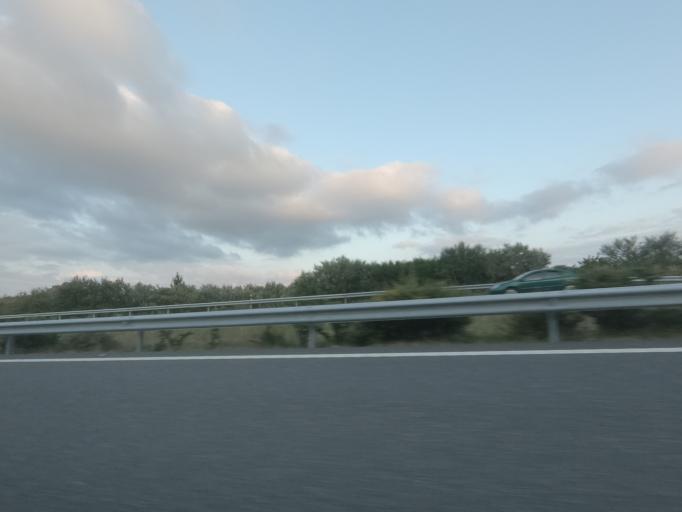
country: ES
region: Galicia
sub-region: Provincia de Pontevedra
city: Covelo
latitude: 42.1869
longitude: -8.3127
